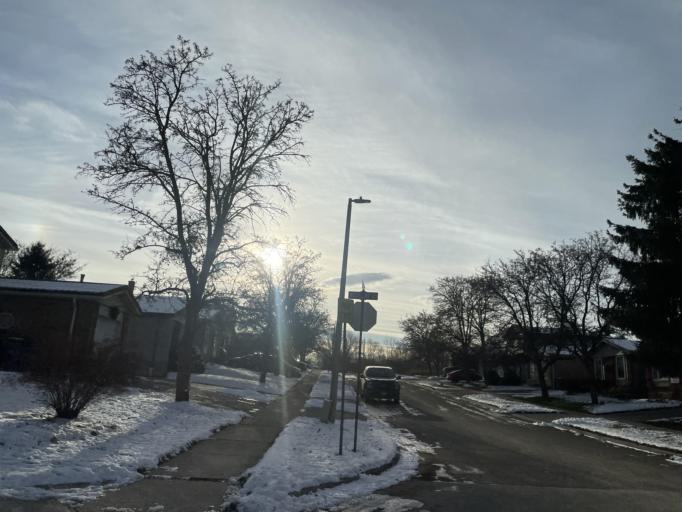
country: CA
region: Ontario
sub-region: Wellington County
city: Guelph
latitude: 43.5141
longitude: -80.2810
